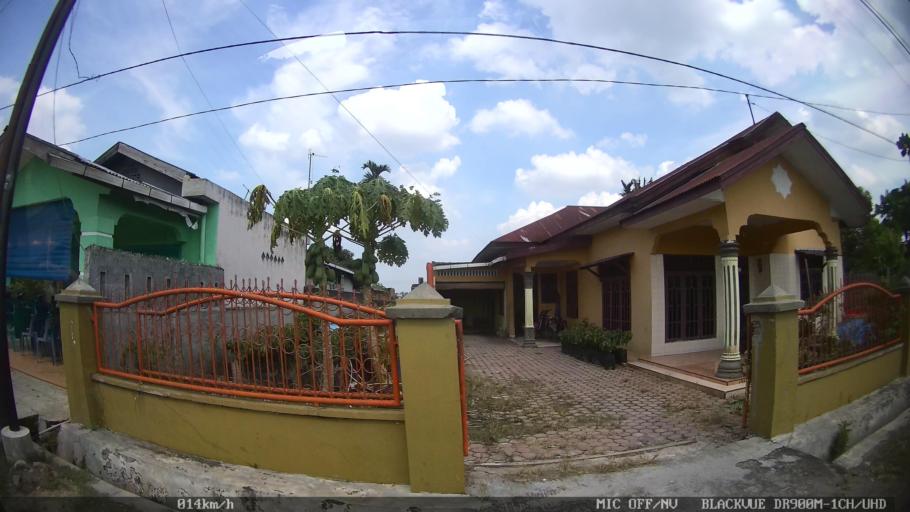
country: ID
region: North Sumatra
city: Binjai
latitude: 3.6258
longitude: 98.5170
